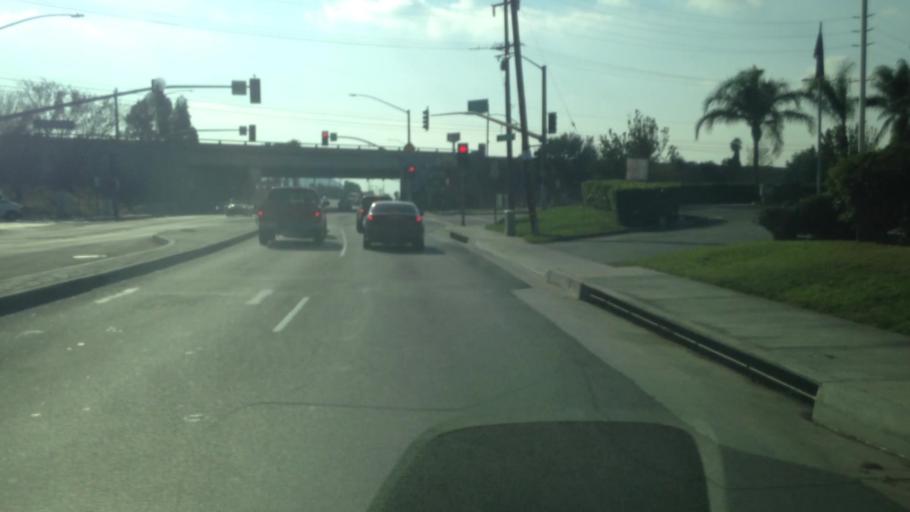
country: US
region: California
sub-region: Riverside County
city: Sunnyslope
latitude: 34.0126
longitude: -117.4326
